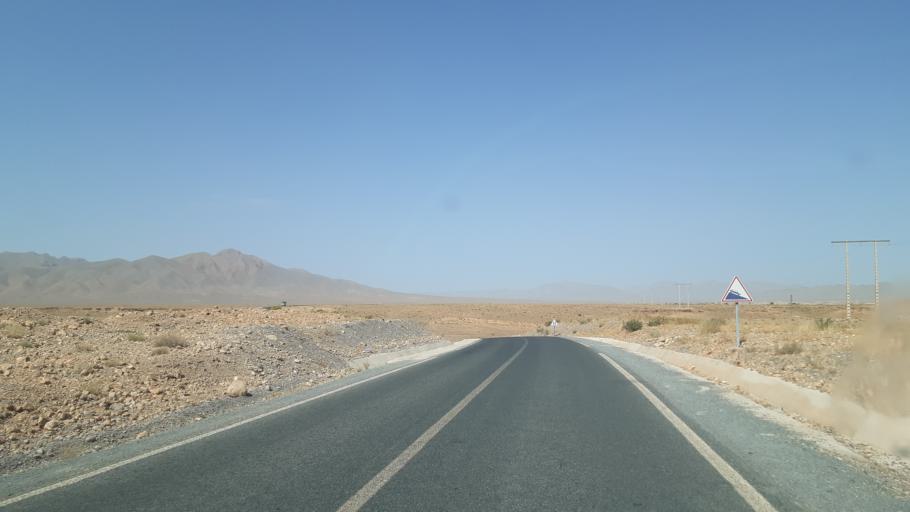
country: MA
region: Meknes-Tafilalet
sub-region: Errachidia
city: Amouguer
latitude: 32.2331
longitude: -4.6458
